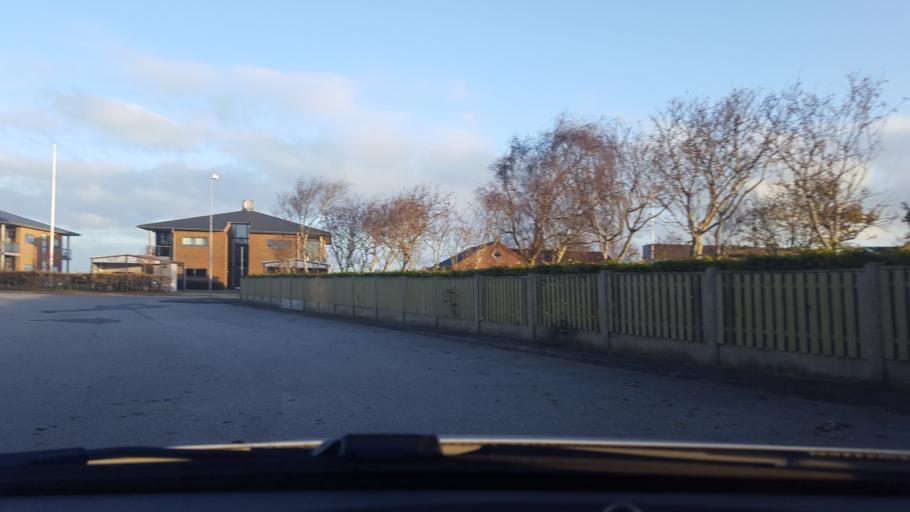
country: DK
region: North Denmark
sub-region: Morso Kommune
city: Nykobing Mors
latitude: 56.7614
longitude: 8.8697
